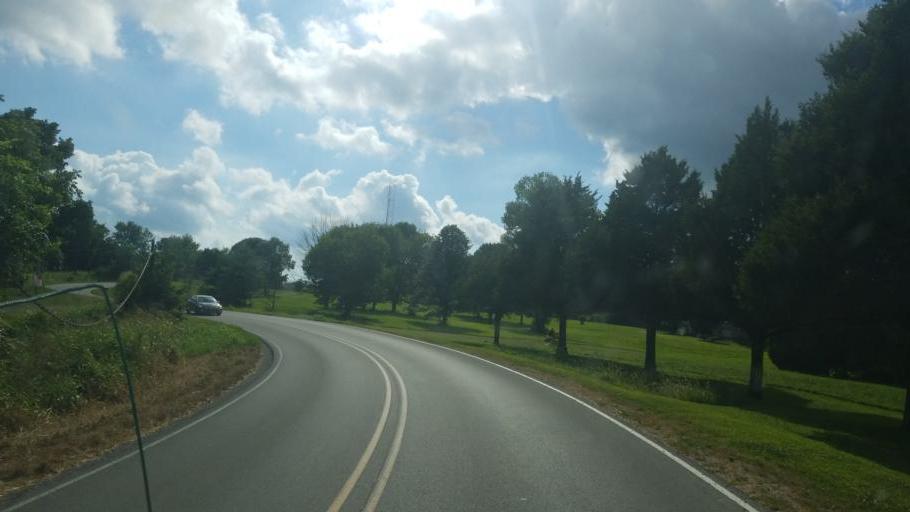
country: US
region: Illinois
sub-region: Union County
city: Cobden
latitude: 37.5483
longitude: -89.2885
